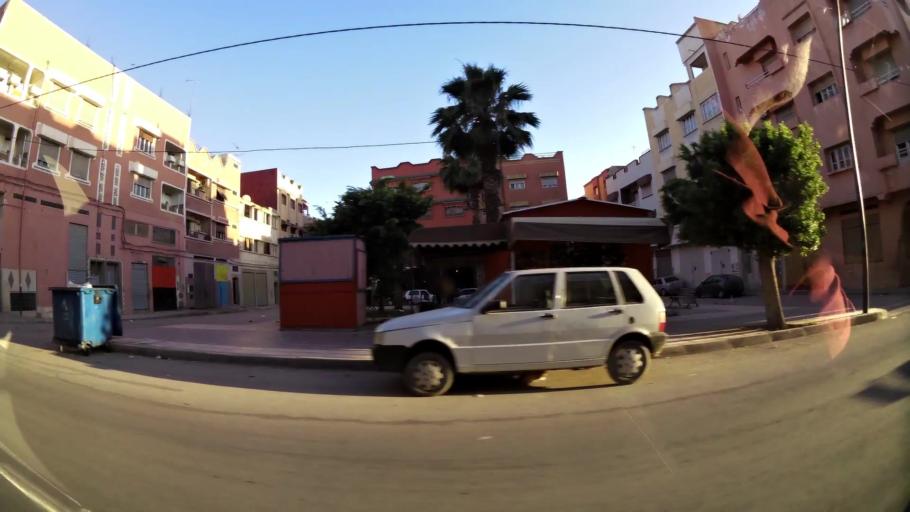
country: MA
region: Oriental
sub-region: Berkane-Taourirt
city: Berkane
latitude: 34.9218
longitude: -2.3329
